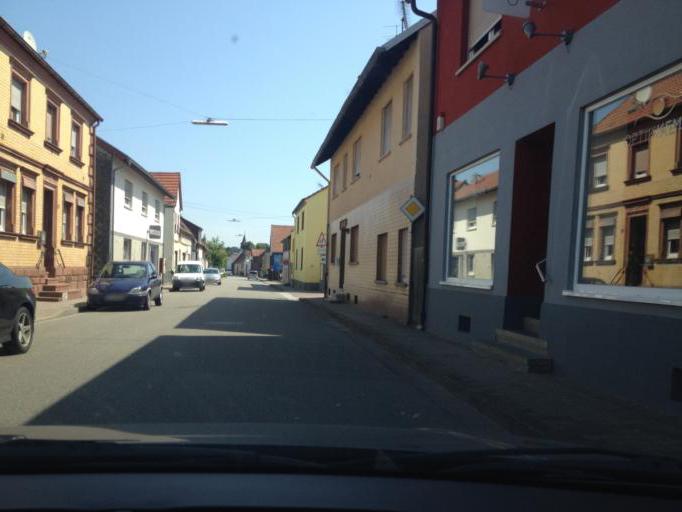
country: DE
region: Rheinland-Pfalz
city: Hutschenhausen
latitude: 49.4244
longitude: 7.4985
